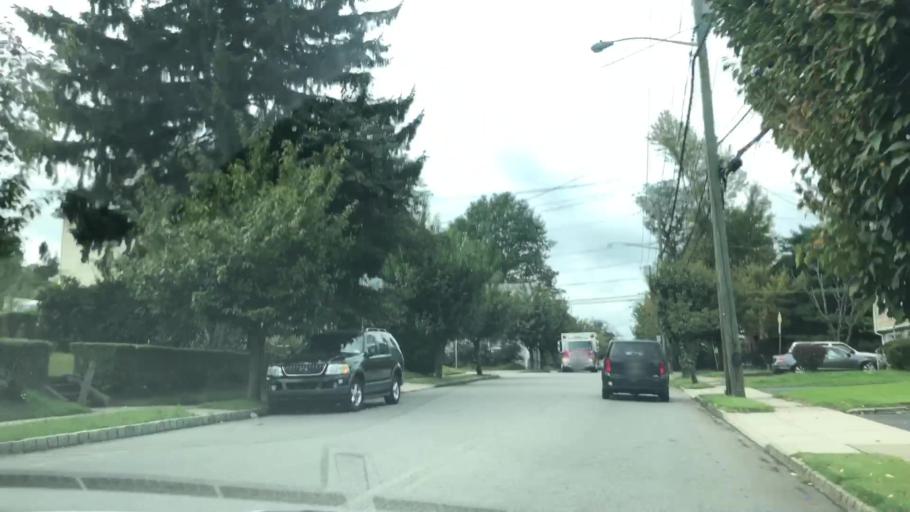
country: US
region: New Jersey
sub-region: Essex County
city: Bloomfield
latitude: 40.7910
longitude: -74.1753
